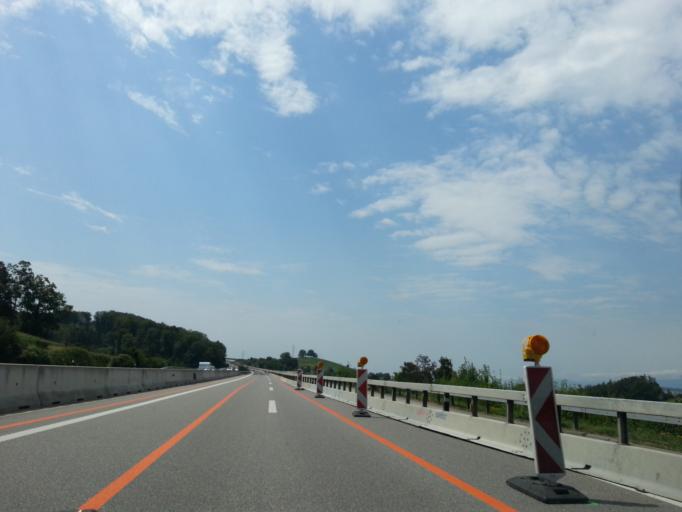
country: CH
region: Fribourg
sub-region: See District
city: Murten
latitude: 46.9405
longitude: 7.1492
